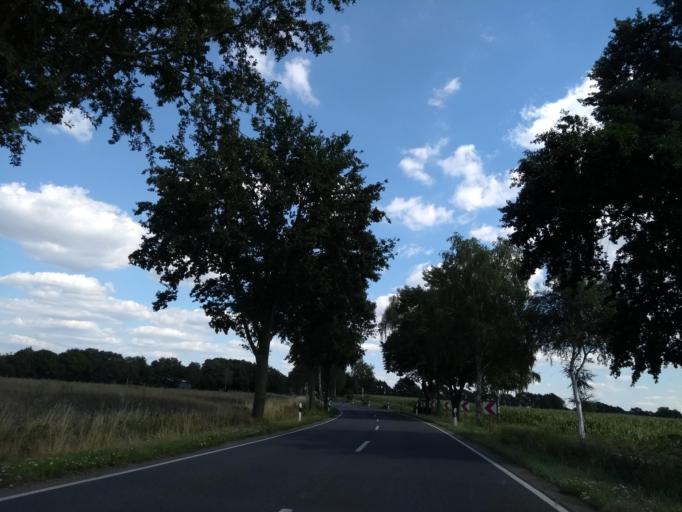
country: DE
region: Lower Saxony
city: Wunstorf
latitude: 52.4531
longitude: 9.4082
